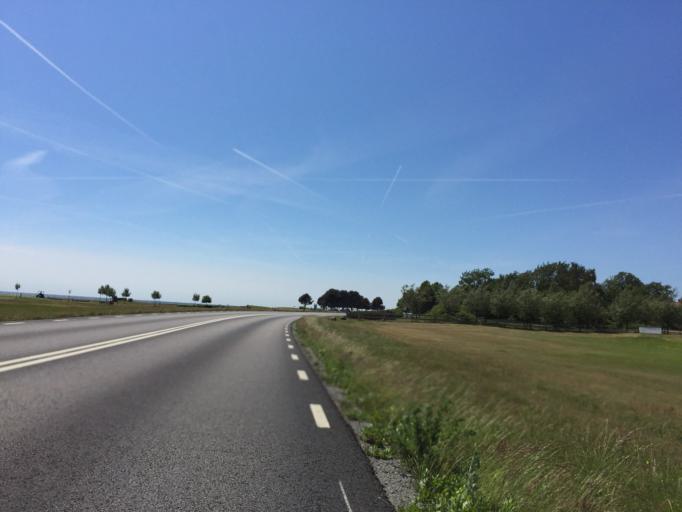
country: SE
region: Skane
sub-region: Trelleborgs Kommun
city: Skare
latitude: 55.3713
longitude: 13.0816
